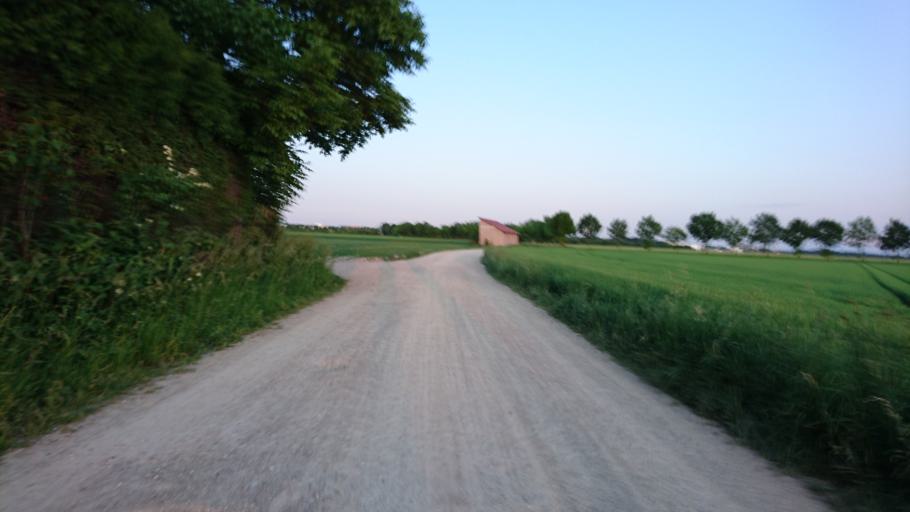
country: DE
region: Bavaria
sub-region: Upper Bavaria
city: Pliening
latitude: 48.1804
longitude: 11.7840
